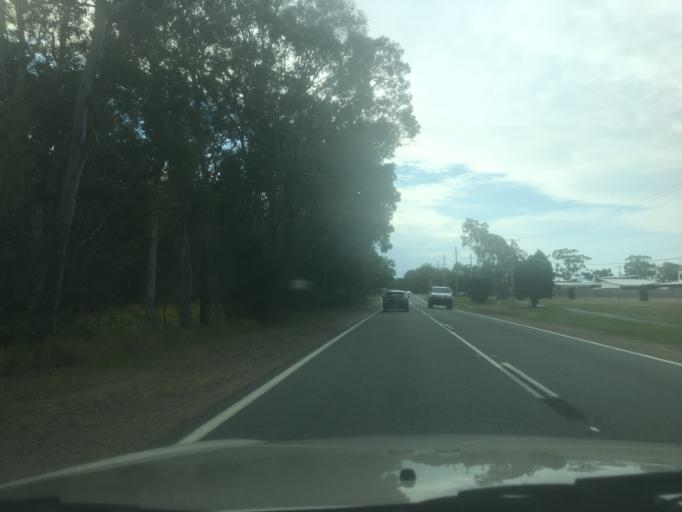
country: AU
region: Queensland
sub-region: Moreton Bay
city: Bongaree
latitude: -27.0709
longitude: 153.1337
